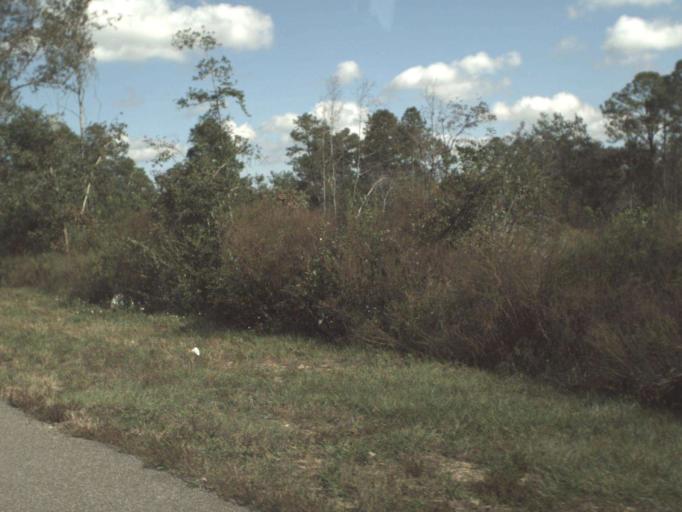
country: US
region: Alabama
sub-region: Geneva County
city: Samson
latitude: 30.9518
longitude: -86.1371
